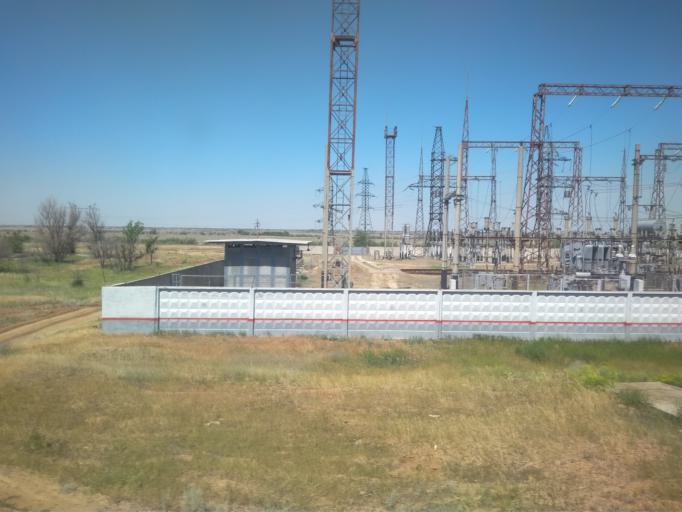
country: RU
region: Volgograd
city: Volgograd
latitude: 48.4144
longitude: 44.3801
